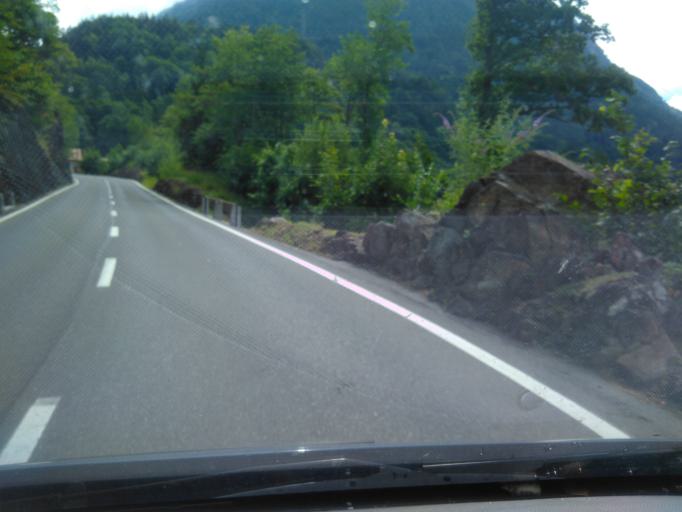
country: CH
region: Bern
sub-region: Interlaken-Oberhasli District
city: Meiringen
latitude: 46.7062
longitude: 8.2338
